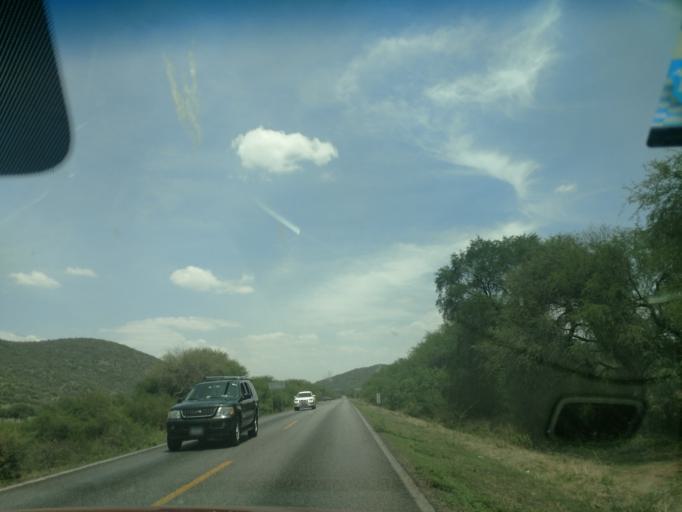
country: MX
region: San Luis Potosi
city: Ciudad Fernandez
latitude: 22.0025
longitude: -100.1444
